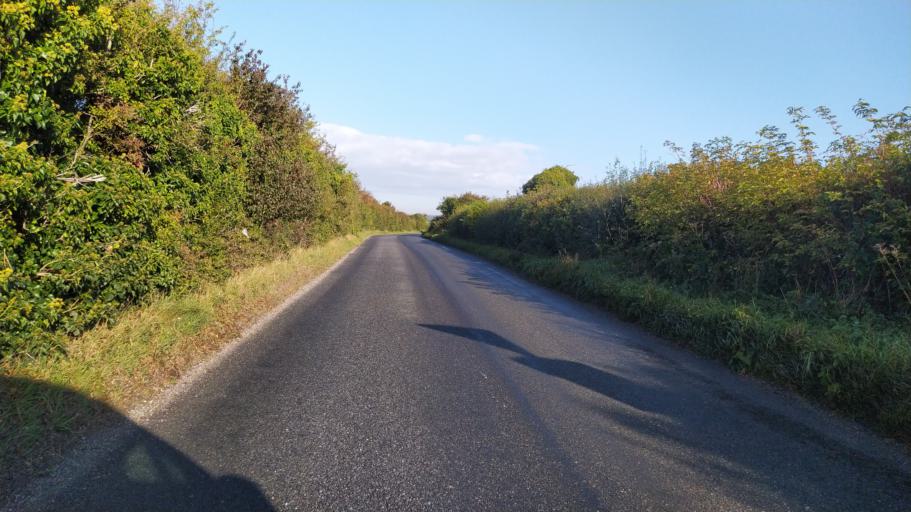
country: GB
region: England
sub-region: Wiltshire
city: Bower Chalke
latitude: 50.9181
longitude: -2.0516
